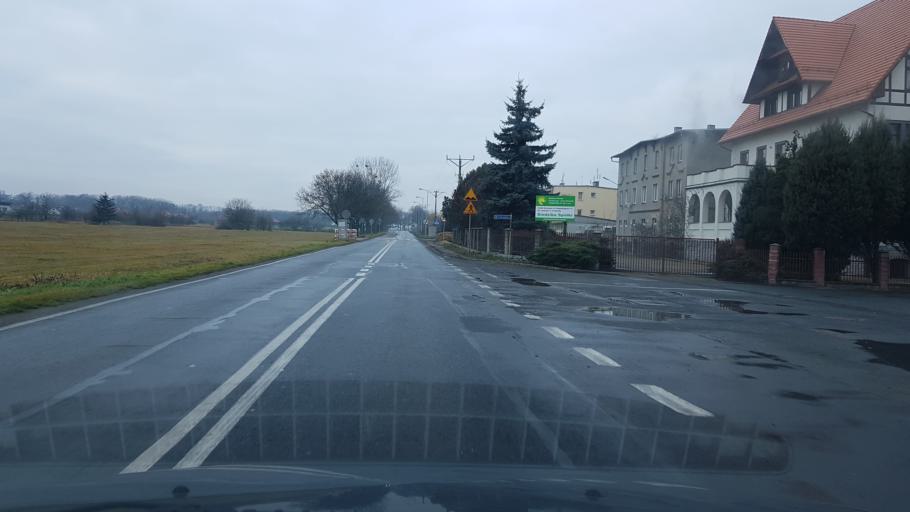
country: PL
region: Lower Silesian Voivodeship
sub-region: Powiat wroclawski
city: Zorawina
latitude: 50.9875
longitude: 17.0141
